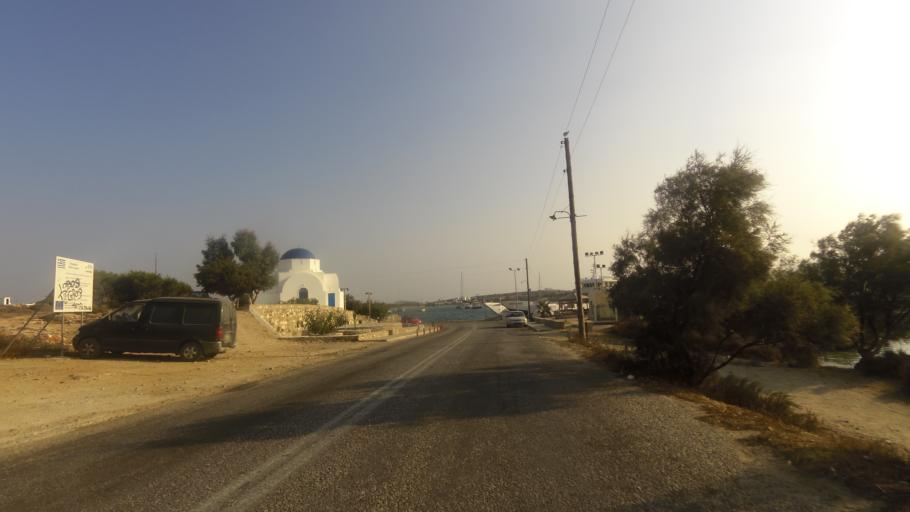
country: GR
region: South Aegean
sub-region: Nomos Kykladon
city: Antiparos
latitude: 37.0387
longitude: 25.0851
